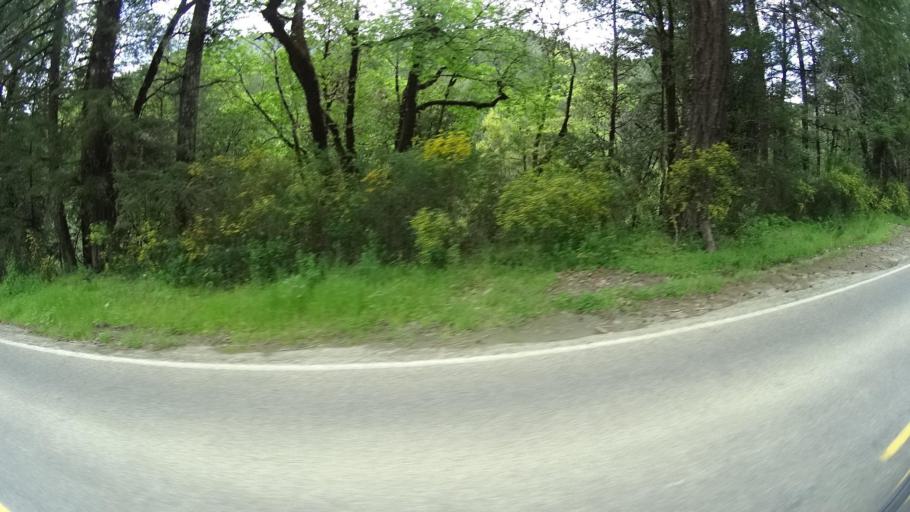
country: US
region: California
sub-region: Humboldt County
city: Redway
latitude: 40.1211
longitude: -123.8832
